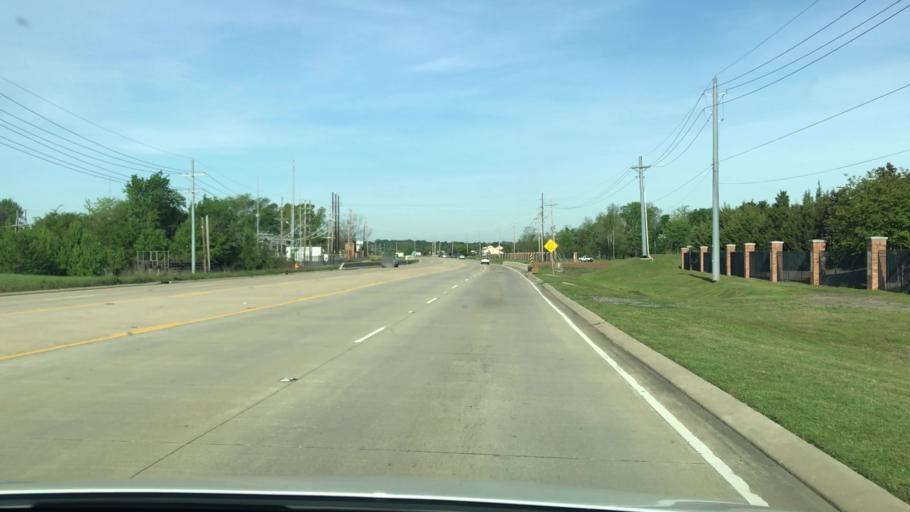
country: US
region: Louisiana
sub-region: Bossier Parish
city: Bossier City
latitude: 32.4011
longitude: -93.7060
